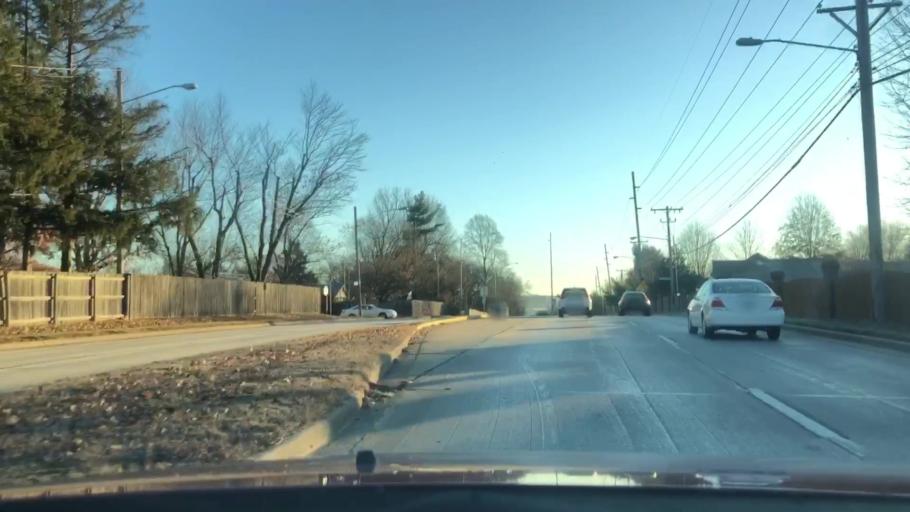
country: US
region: Missouri
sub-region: Greene County
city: Springfield
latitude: 37.1587
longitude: -93.2470
